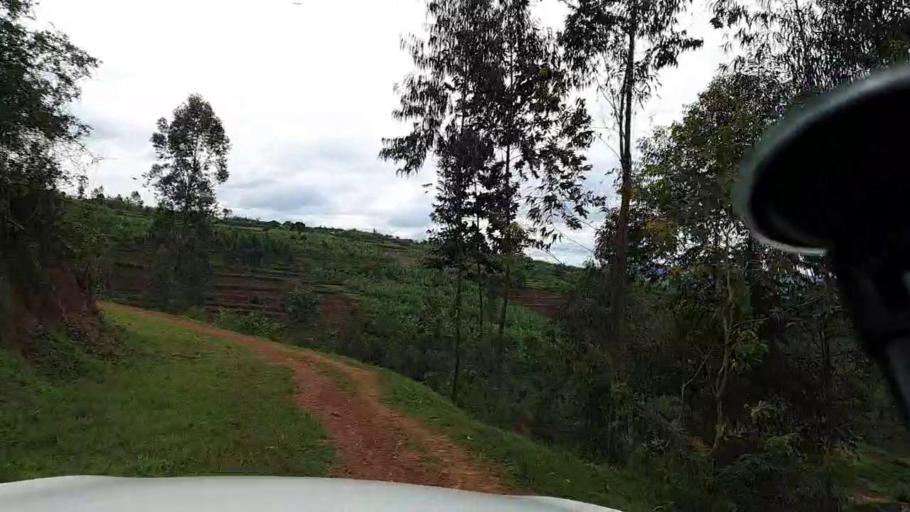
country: RW
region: Southern Province
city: Gitarama
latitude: -2.0802
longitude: 29.6442
